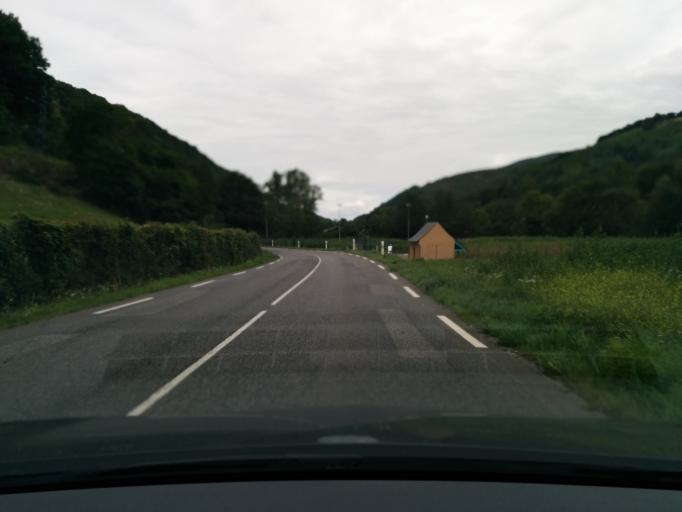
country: FR
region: Midi-Pyrenees
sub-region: Departement des Hautes-Pyrenees
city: La Barthe-de-Neste
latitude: 42.9766
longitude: 0.3762
